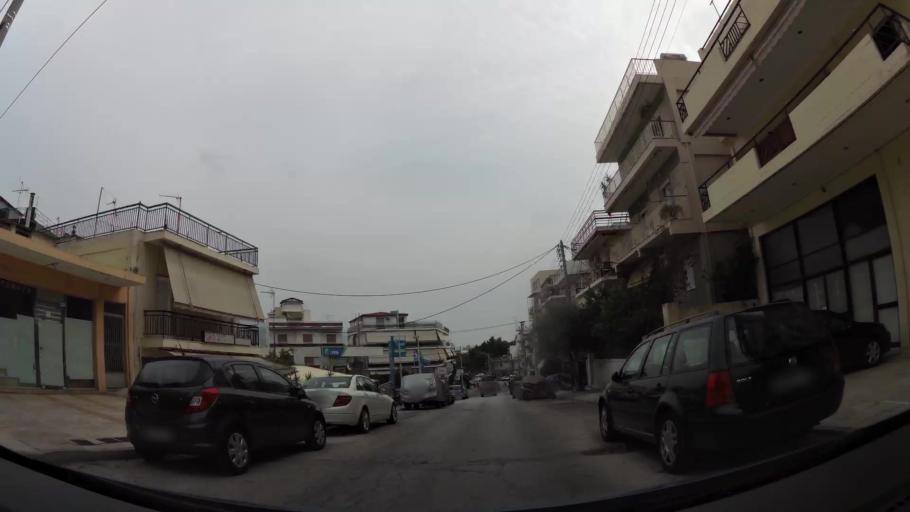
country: GR
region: Attica
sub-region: Nomarchia Athinas
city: Agios Dimitrios
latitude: 37.9242
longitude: 23.7383
